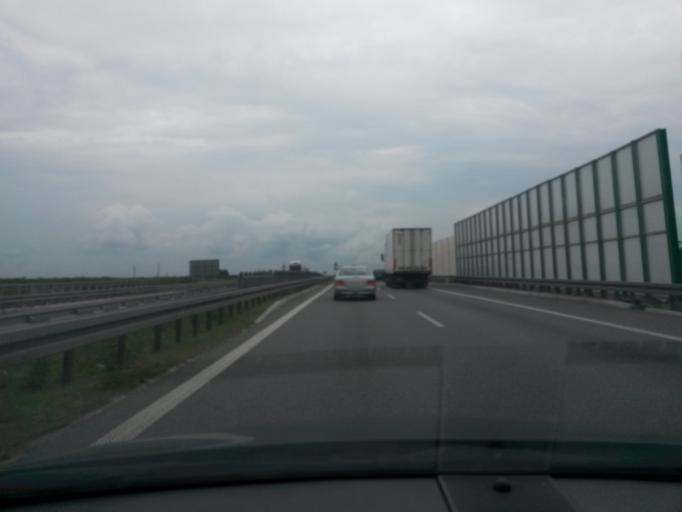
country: PL
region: Lodz Voivodeship
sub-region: Powiat skierniewicki
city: Kowiesy
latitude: 51.9125
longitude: 20.4472
